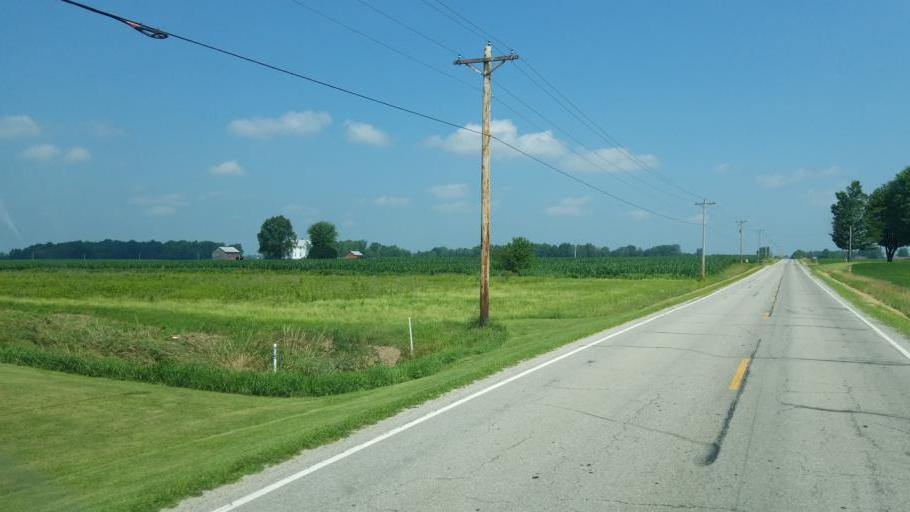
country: US
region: Ohio
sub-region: Huron County
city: Willard
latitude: 40.9754
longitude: -82.8534
